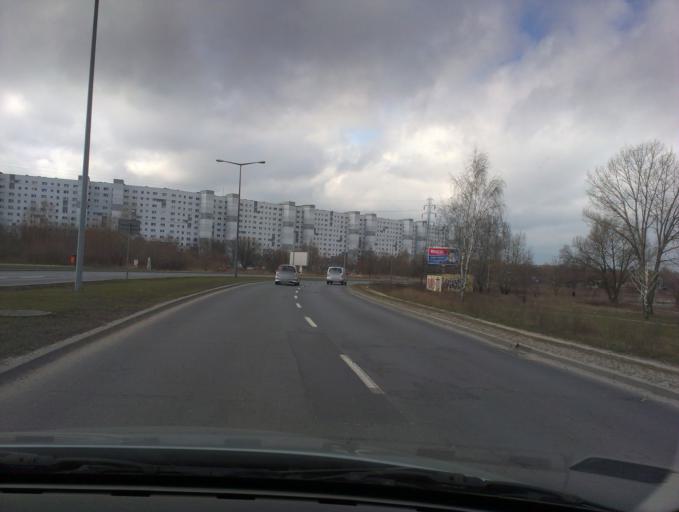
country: PL
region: Greater Poland Voivodeship
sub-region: Poznan
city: Poznan
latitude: 52.3866
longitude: 16.9942
